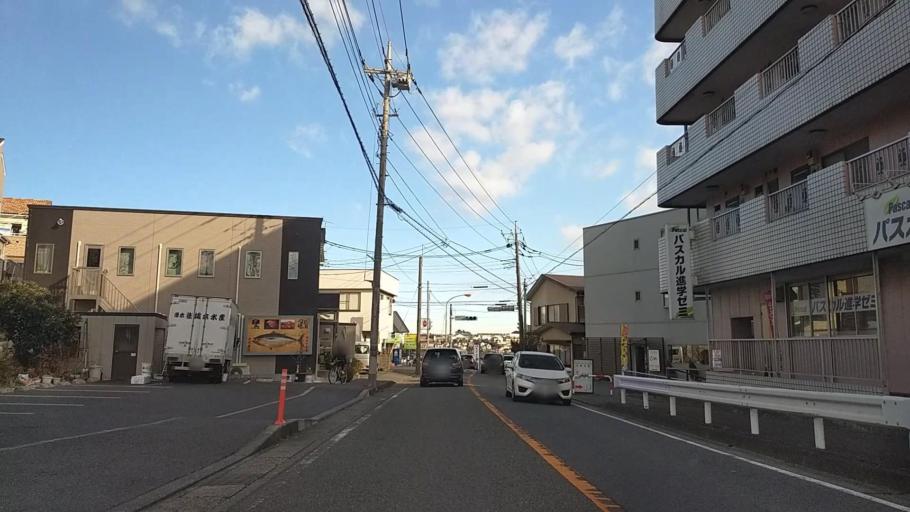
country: JP
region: Kanagawa
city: Atsugi
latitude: 35.4355
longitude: 139.3378
